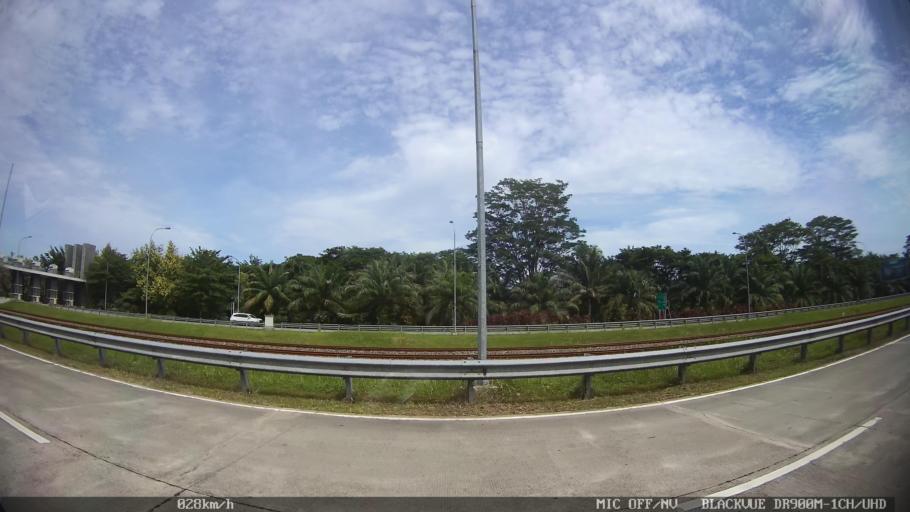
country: ID
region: North Sumatra
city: Percut
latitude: 3.6144
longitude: 98.8584
